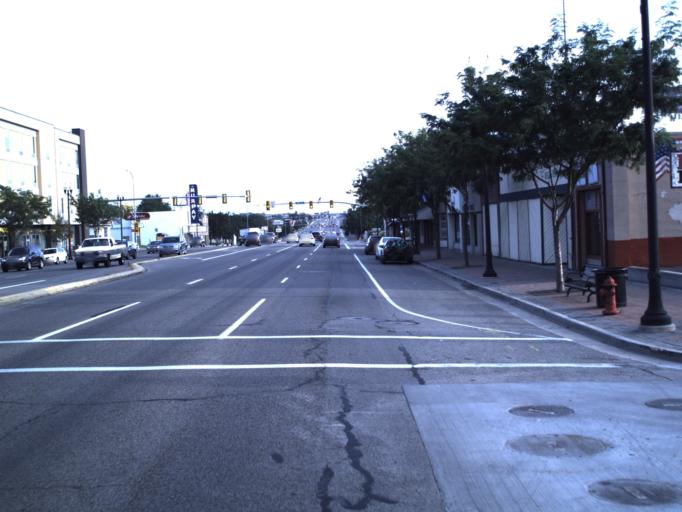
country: US
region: Utah
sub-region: Salt Lake County
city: Murray
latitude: 40.6656
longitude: -111.8884
